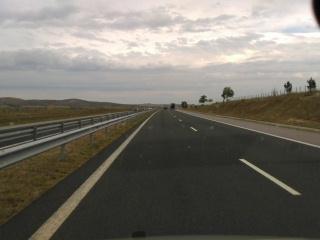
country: BG
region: Sliven
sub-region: Obshtina Sliven
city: Kermen
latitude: 42.5023
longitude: 26.3016
